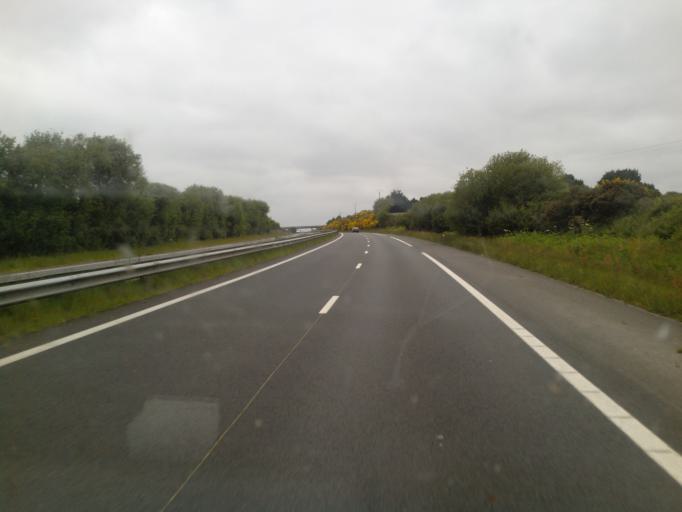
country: FR
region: Brittany
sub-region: Departement du Finistere
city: Guerlesquin
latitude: 48.5638
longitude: -3.5275
